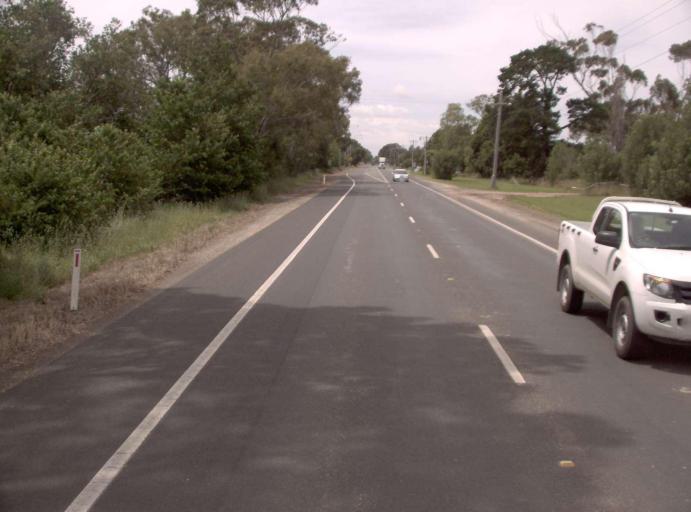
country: AU
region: Victoria
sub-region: Wellington
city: Sale
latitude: -38.0852
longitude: 147.0574
